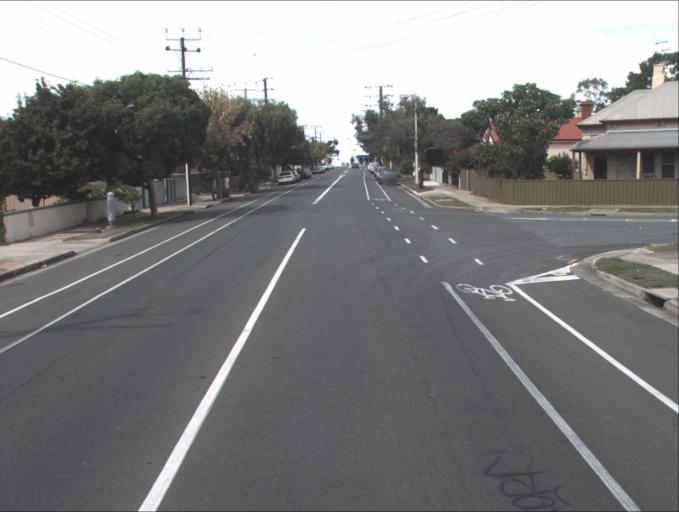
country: AU
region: South Australia
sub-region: Port Adelaide Enfield
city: Birkenhead
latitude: -34.8373
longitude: 138.4887
